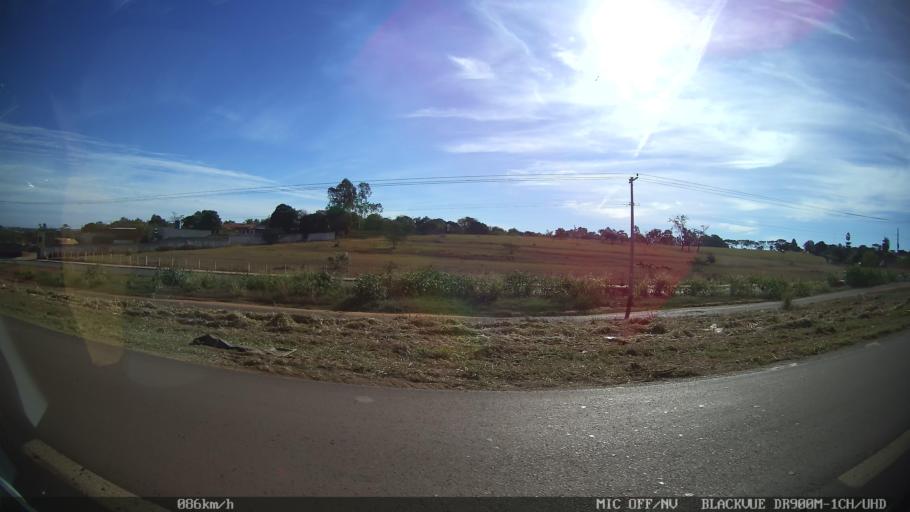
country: BR
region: Sao Paulo
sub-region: Sao Jose Do Rio Preto
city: Sao Jose do Rio Preto
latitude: -20.7496
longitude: -49.3411
